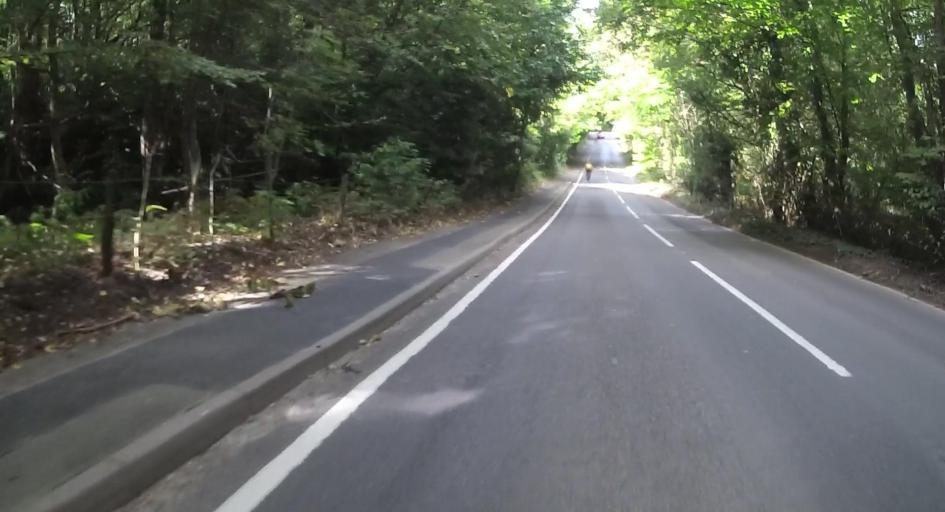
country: GB
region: England
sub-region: Surrey
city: Virginia Water
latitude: 51.3835
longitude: -0.5738
